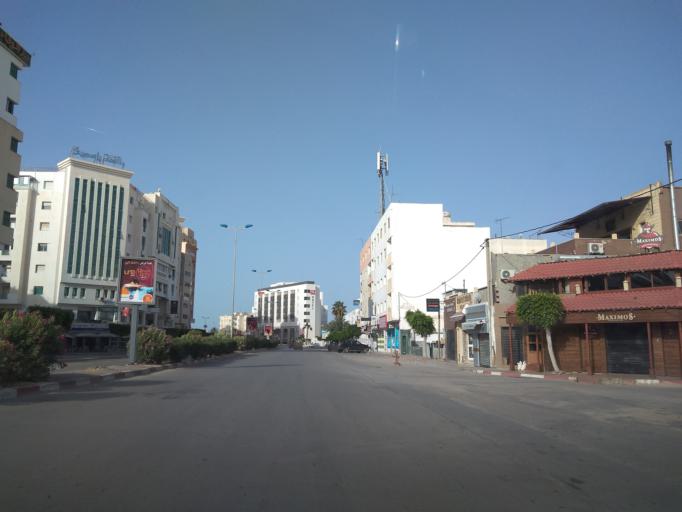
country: TN
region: Safaqis
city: Sfax
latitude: 34.7382
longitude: 10.7504
